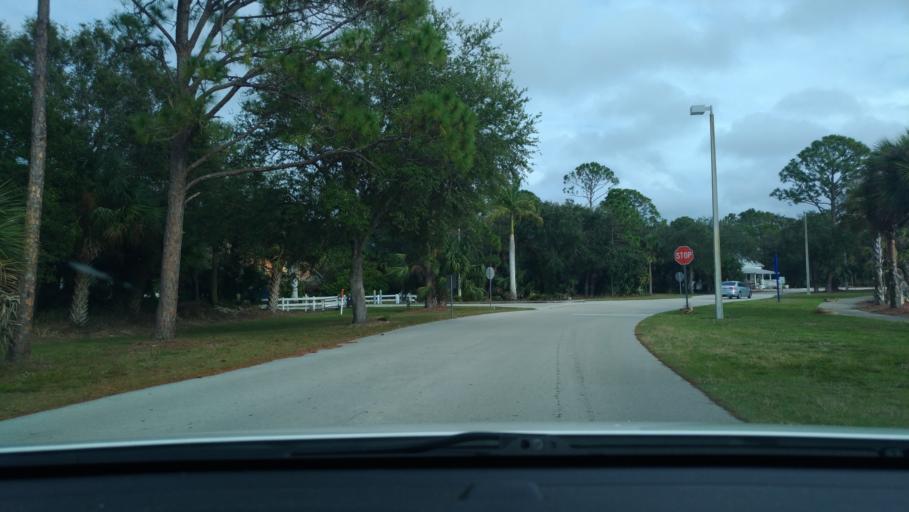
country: US
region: Florida
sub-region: Lee County
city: Estero
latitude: 26.4294
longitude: -81.8004
